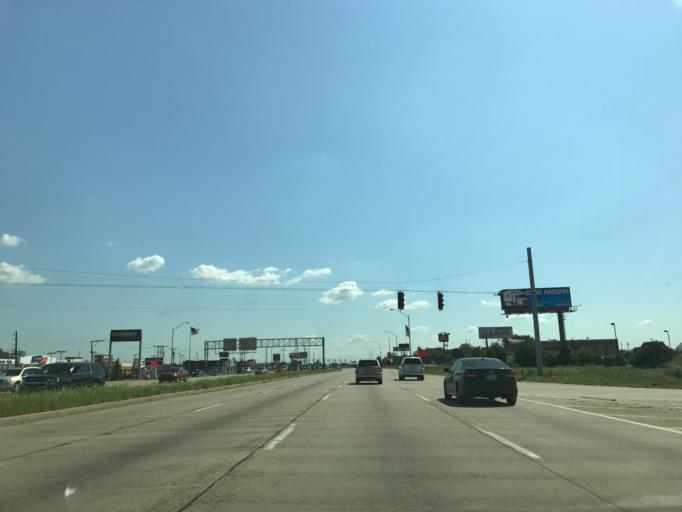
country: US
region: Indiana
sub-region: Lake County
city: Merrillville
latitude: 41.4710
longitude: -87.3221
